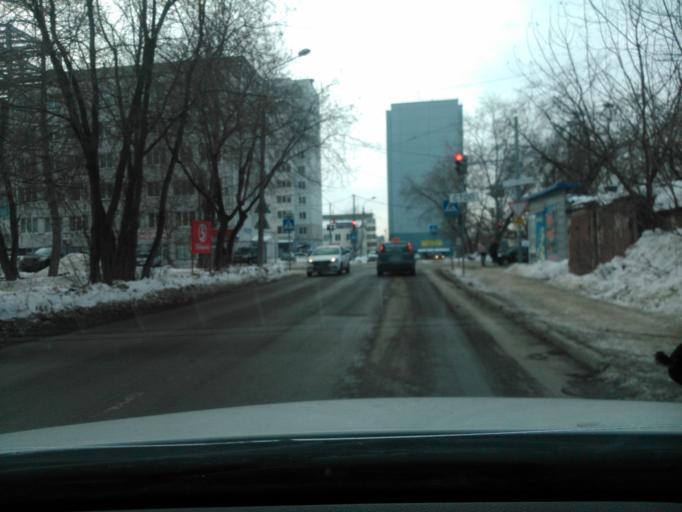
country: RU
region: Perm
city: Perm
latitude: 57.9953
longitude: 56.2424
